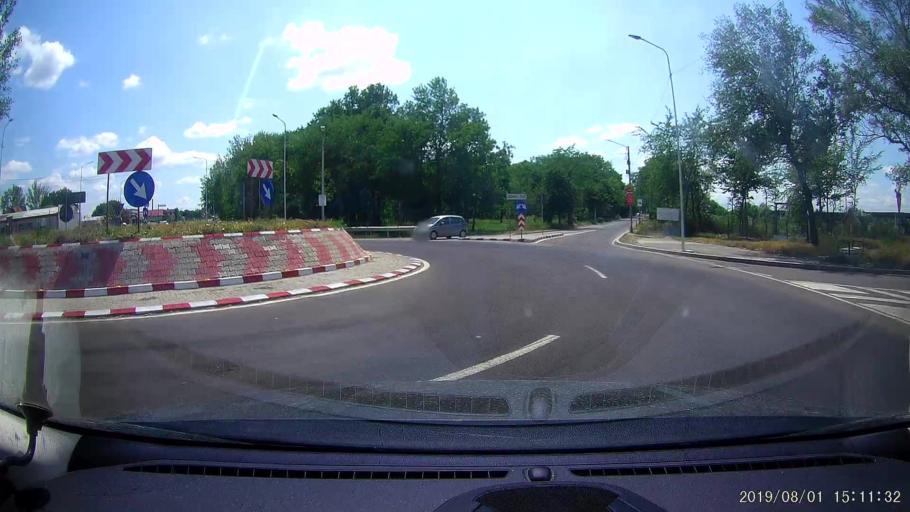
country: RO
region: Braila
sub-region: Comuna Chiscani
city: Chiscani
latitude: 45.2166
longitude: 27.9230
